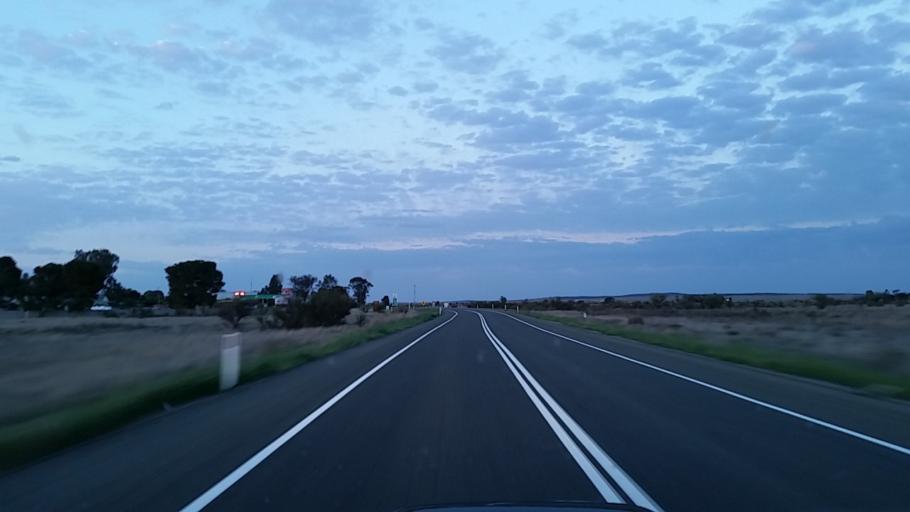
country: AU
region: South Australia
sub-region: Peterborough
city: Peterborough
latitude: -33.1556
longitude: 138.9209
